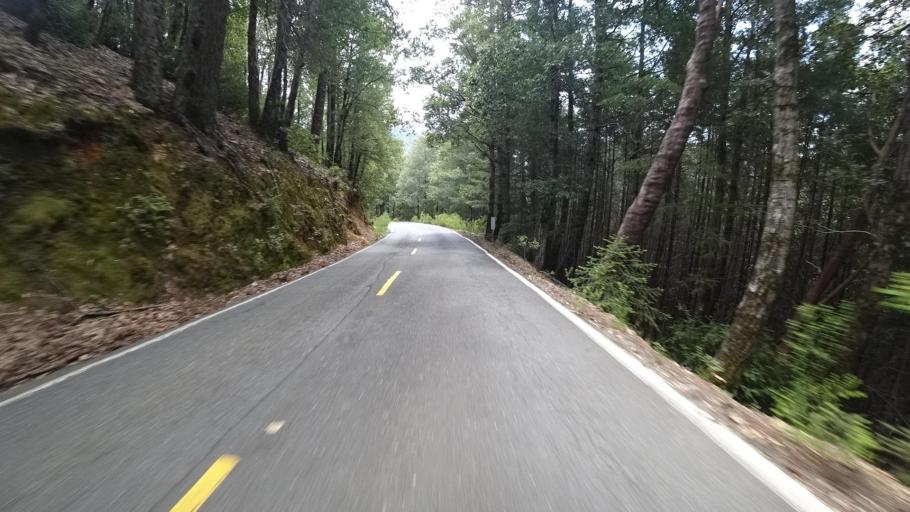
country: US
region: California
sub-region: Humboldt County
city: Redway
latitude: 40.0401
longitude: -124.0235
